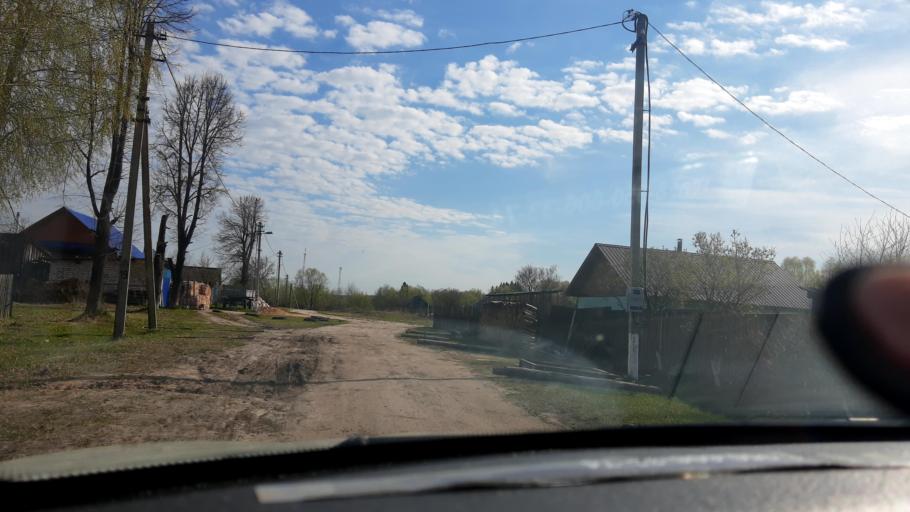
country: RU
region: Mariy-El
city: Kilemary
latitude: 56.7821
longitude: 46.8659
